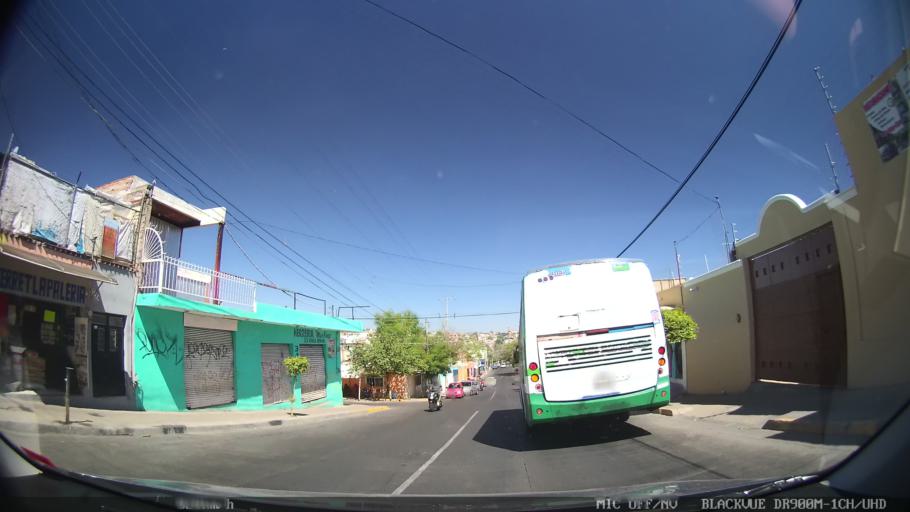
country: MX
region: Jalisco
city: Tlaquepaque
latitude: 20.6890
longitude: -103.2798
